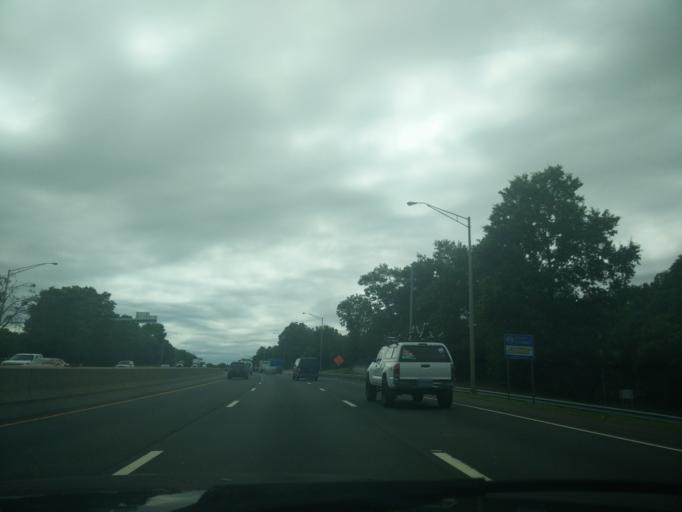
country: US
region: Connecticut
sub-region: New Haven County
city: City of Milford (balance)
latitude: 41.2144
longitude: -73.0871
